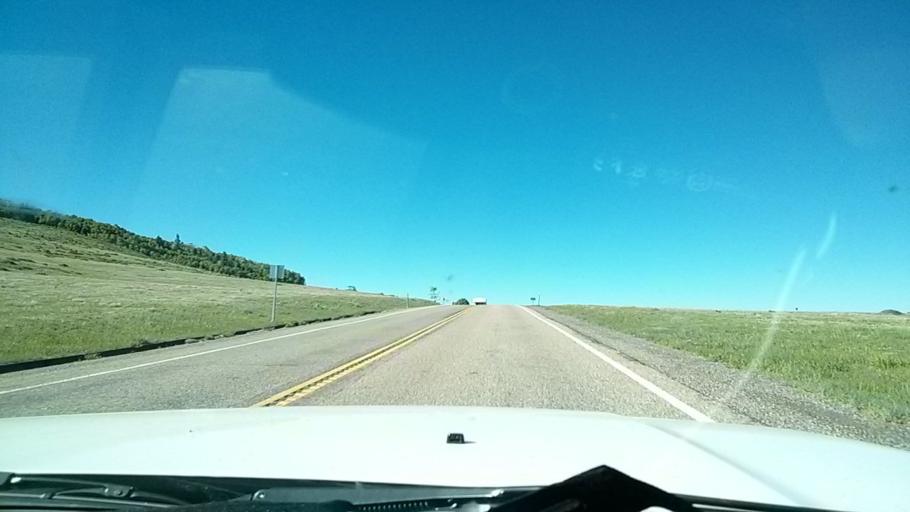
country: US
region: Utah
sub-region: Wayne County
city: Loa
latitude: 38.0350
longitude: -111.3314
